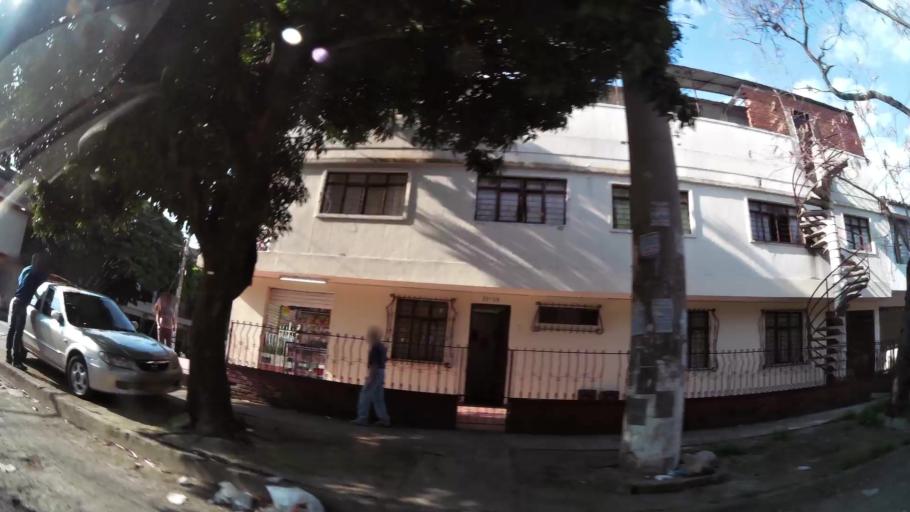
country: CO
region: Valle del Cauca
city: Cali
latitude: 3.4162
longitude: -76.5344
